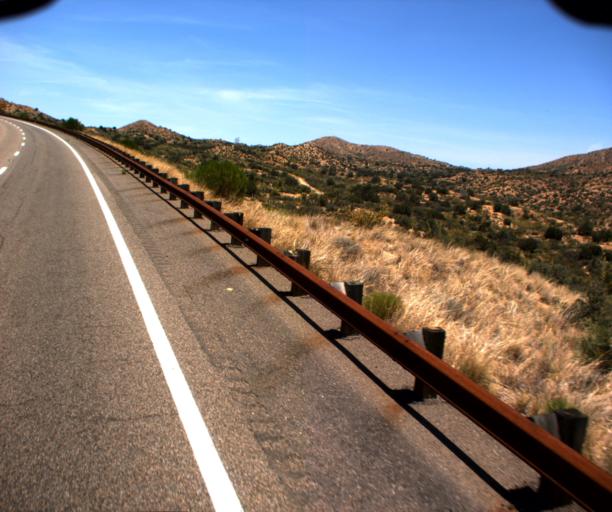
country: US
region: Arizona
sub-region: Gila County
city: Miami
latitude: 33.5337
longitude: -110.9198
